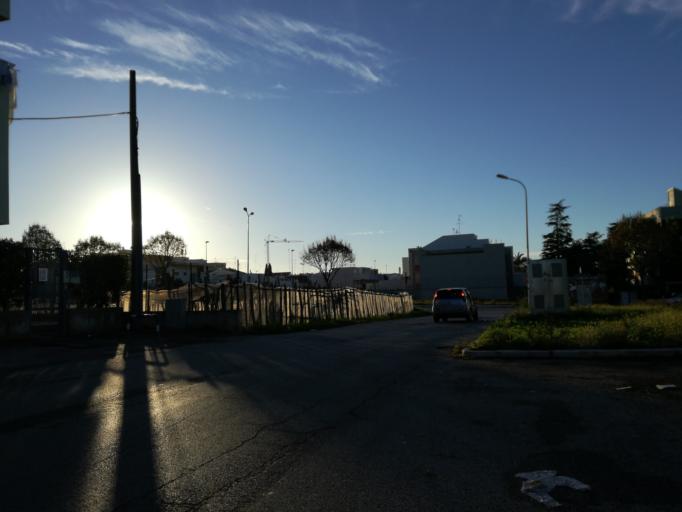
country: IT
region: Apulia
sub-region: Provincia di Bari
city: Adelfia
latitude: 41.0068
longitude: 16.8703
